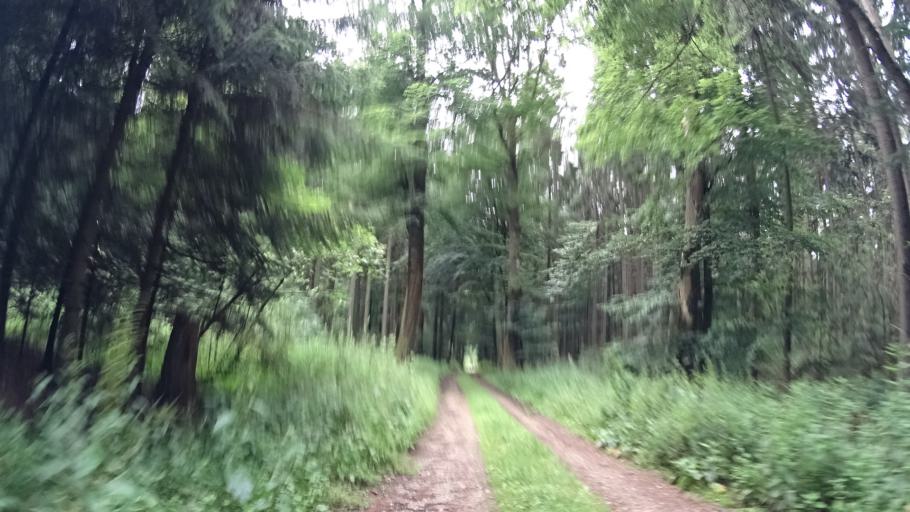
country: DE
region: Bavaria
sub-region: Upper Bavaria
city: Stammham
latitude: 48.8730
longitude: 11.4335
